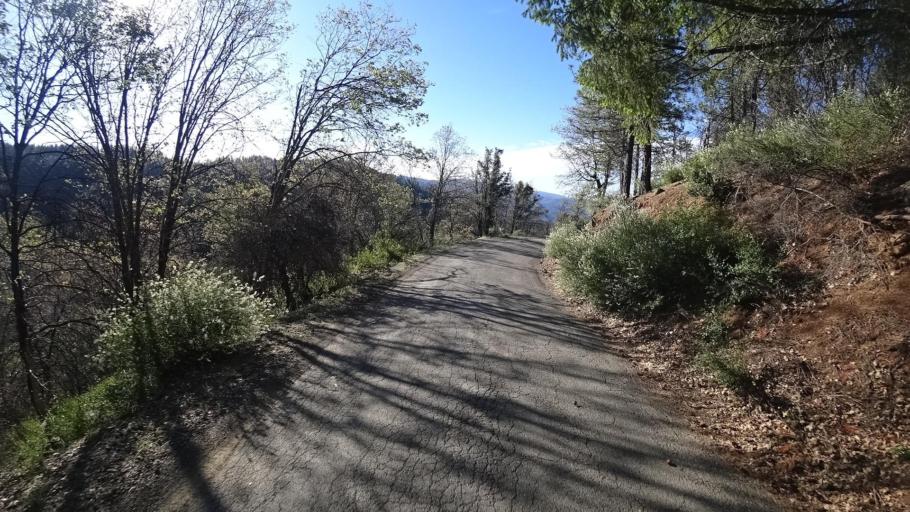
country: US
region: California
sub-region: Lake County
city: Upper Lake
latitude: 39.2850
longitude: -122.9266
